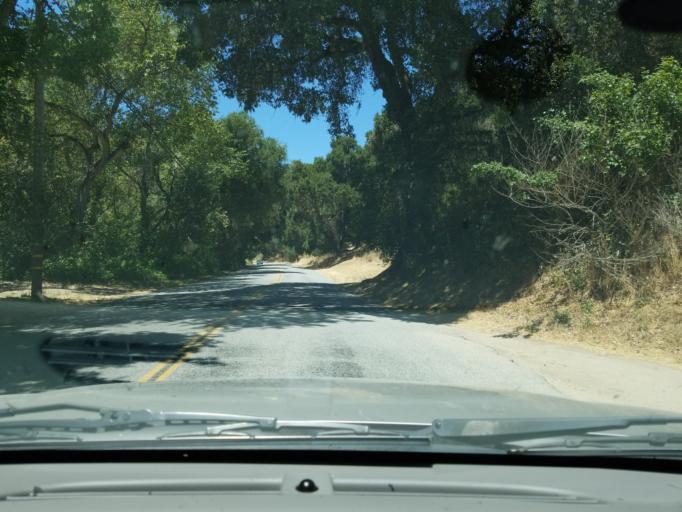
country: US
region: California
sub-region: Monterey County
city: Carmel Valley Village
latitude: 36.4532
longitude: -121.6959
